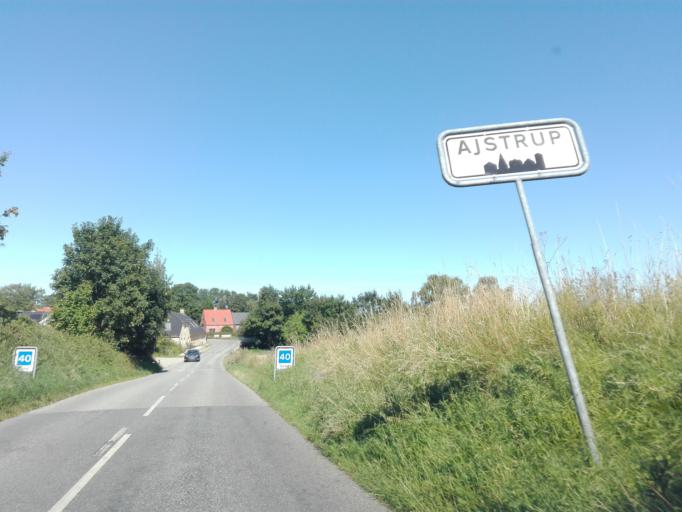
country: DK
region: Central Jutland
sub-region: Arhus Kommune
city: Beder
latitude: 56.0347
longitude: 10.2389
